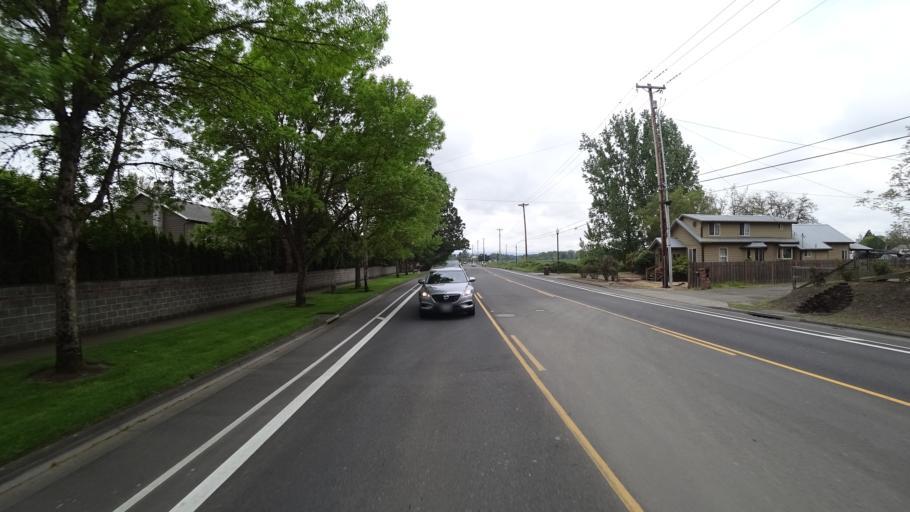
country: US
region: Oregon
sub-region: Washington County
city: Hillsboro
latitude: 45.5500
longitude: -122.9700
